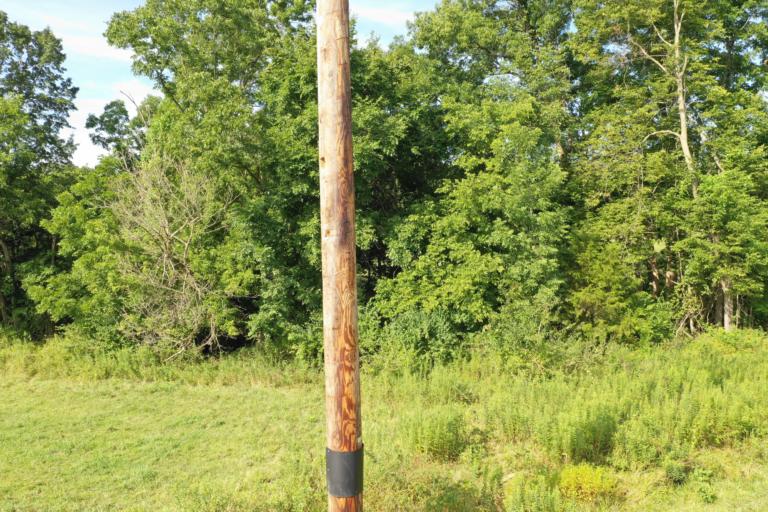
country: US
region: Missouri
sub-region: Callaway County
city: Holts Summit
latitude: 38.5342
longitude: -92.0484
